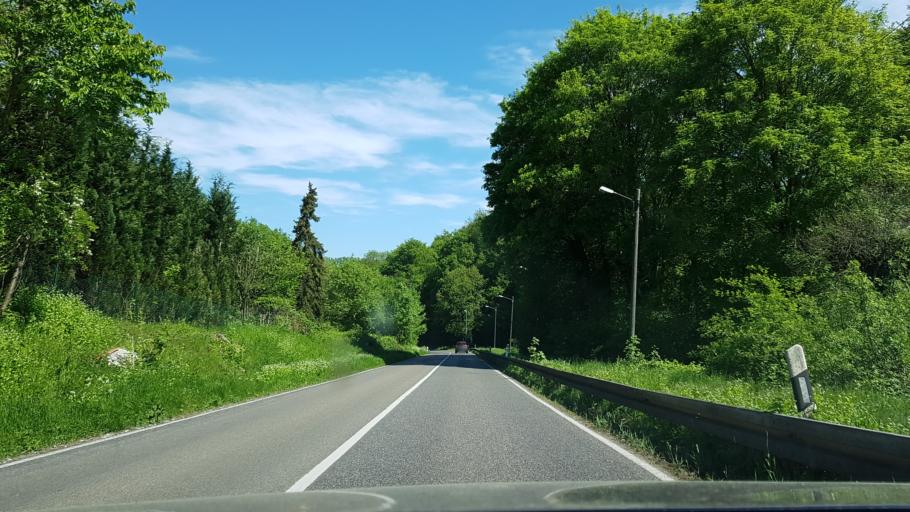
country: DE
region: North Rhine-Westphalia
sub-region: Regierungsbezirk Dusseldorf
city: Heiligenhaus
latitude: 51.3034
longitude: 6.9451
